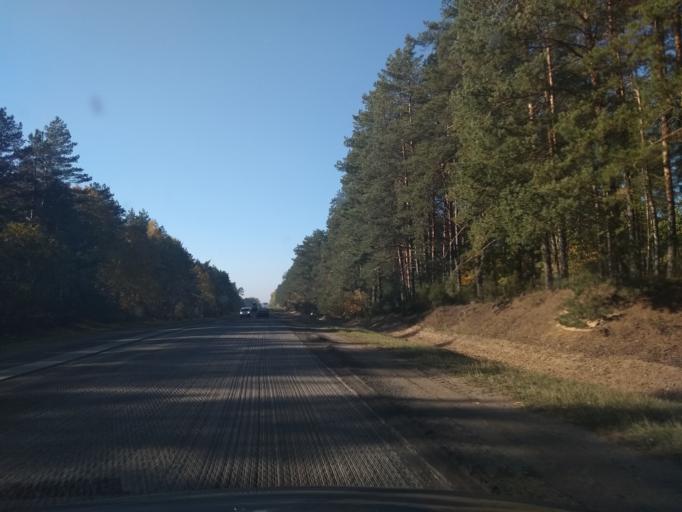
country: BY
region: Grodnenskaya
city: Zhyrovichy
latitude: 53.0615
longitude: 25.4240
